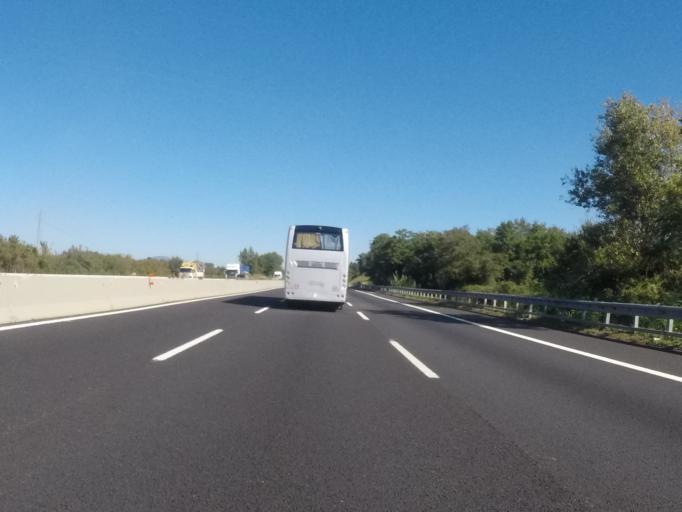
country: IT
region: Campania
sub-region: Provincia di Caserta
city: Teano
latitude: 41.2456
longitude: 14.0924
